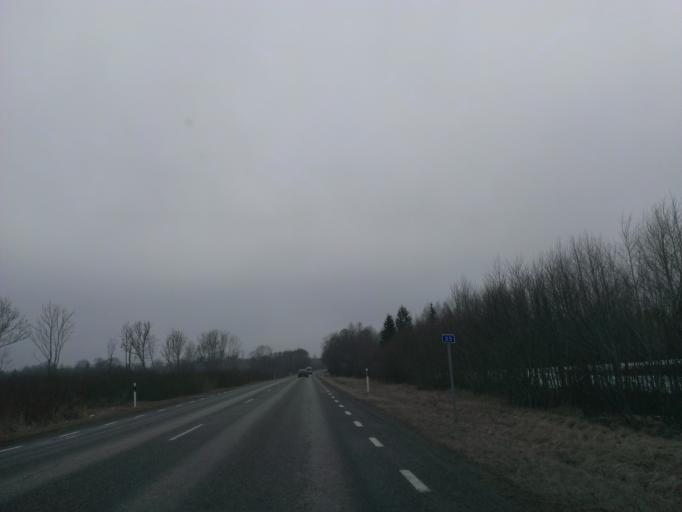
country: EE
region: Paernumaa
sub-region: Audru vald
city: Audru
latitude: 58.4803
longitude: 24.1677
